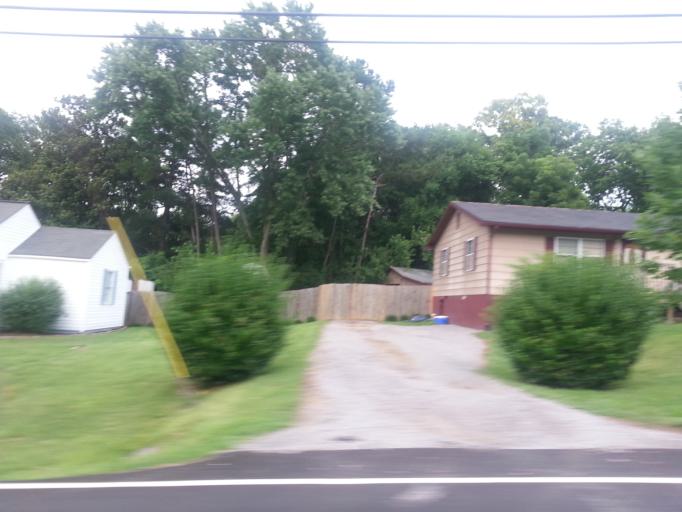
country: US
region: Tennessee
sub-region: Knox County
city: Knoxville
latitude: 36.0133
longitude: -83.8992
